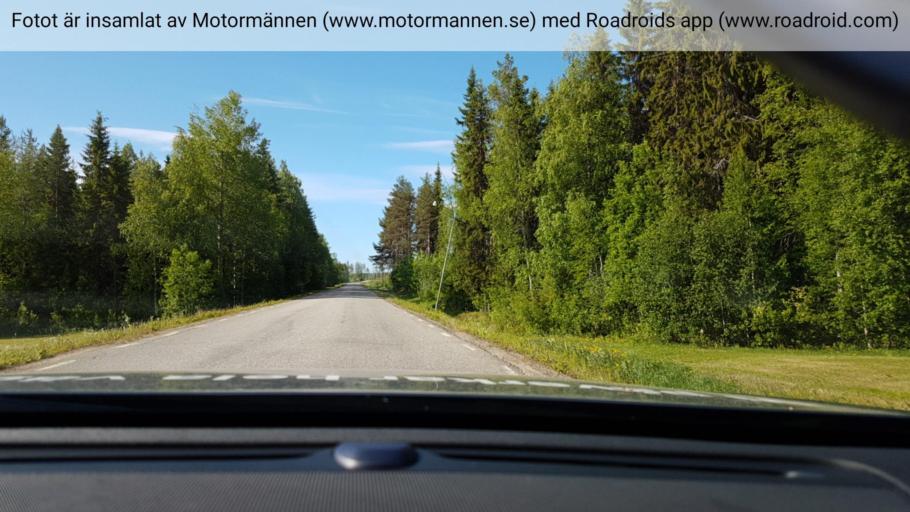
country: SE
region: Vaesterbotten
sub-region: Bjurholms Kommun
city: Bjurholm
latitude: 64.1433
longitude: 19.3125
